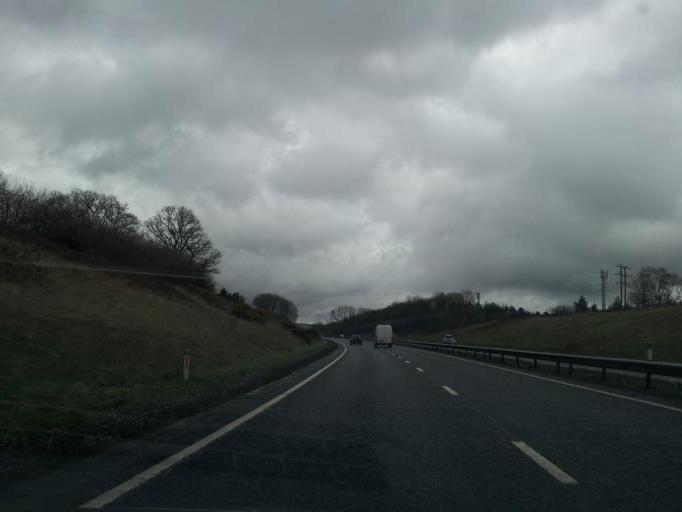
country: GB
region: England
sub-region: Wiltshire
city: Kilmington
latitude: 51.0688
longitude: -2.3289
